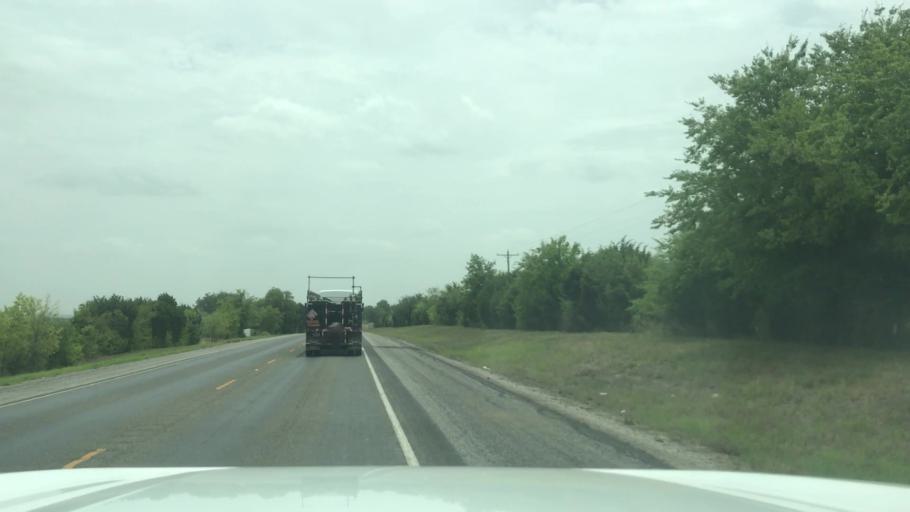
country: US
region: Texas
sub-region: Bosque County
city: Meridian
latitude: 31.8688
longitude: -97.6353
